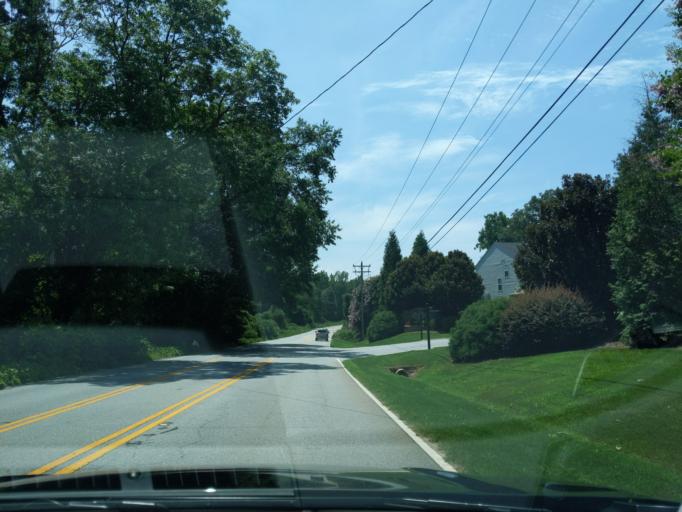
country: US
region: South Carolina
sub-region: Greenville County
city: Five Forks
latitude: 34.7740
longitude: -82.2088
